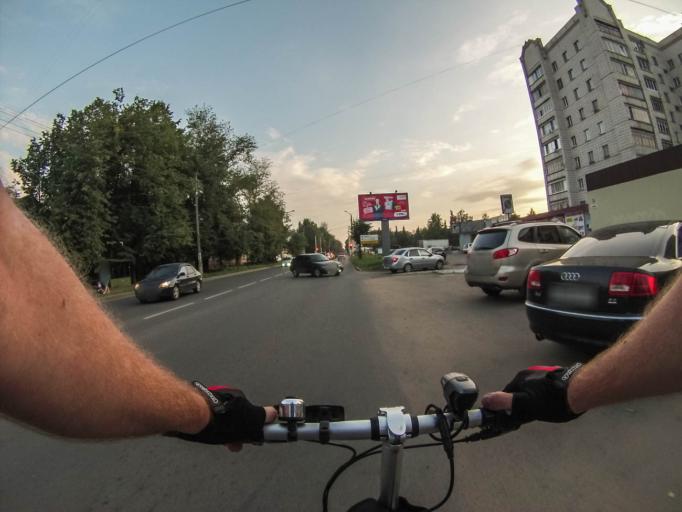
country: RU
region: Kostroma
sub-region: Kostromskoy Rayon
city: Kostroma
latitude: 57.7903
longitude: 40.9448
